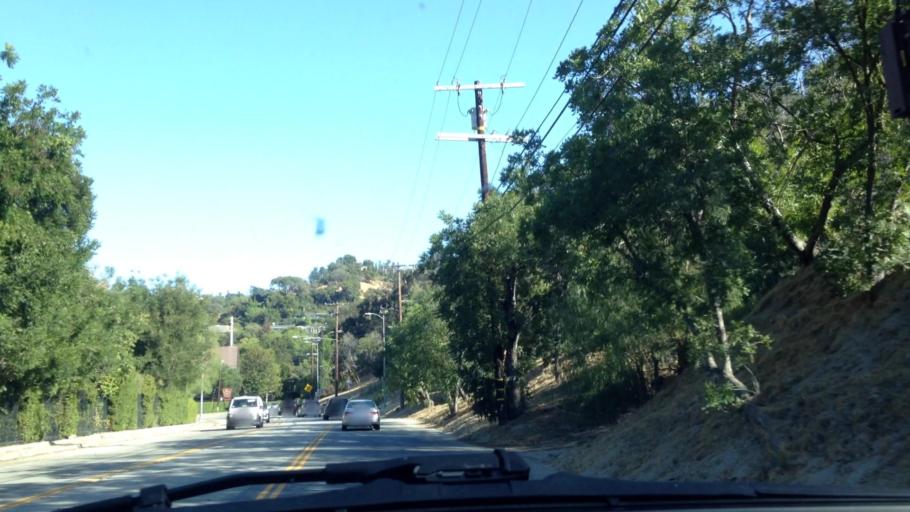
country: US
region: California
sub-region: Los Angeles County
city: Sherman Oaks
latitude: 34.1386
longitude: -118.4134
